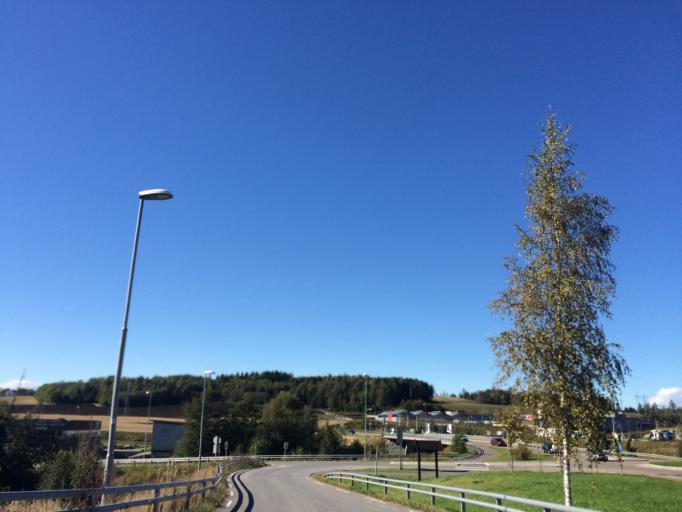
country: NO
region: Akershus
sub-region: Ski
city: Ski
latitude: 59.7239
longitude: 10.7885
